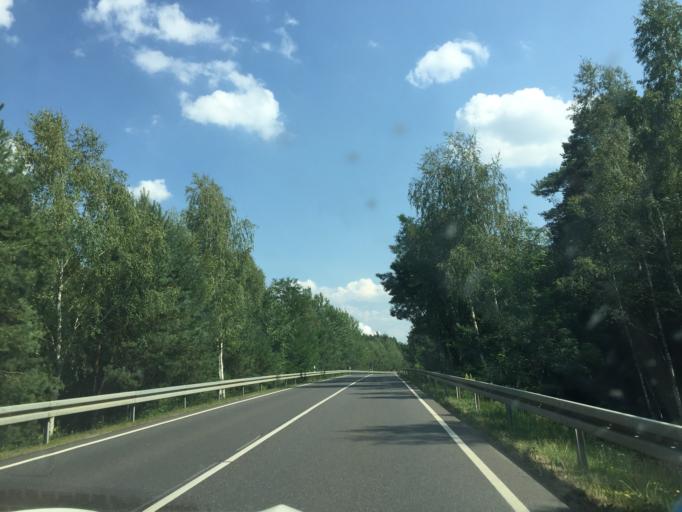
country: DE
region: Saxony
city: Boxberg
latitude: 51.4028
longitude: 14.5313
